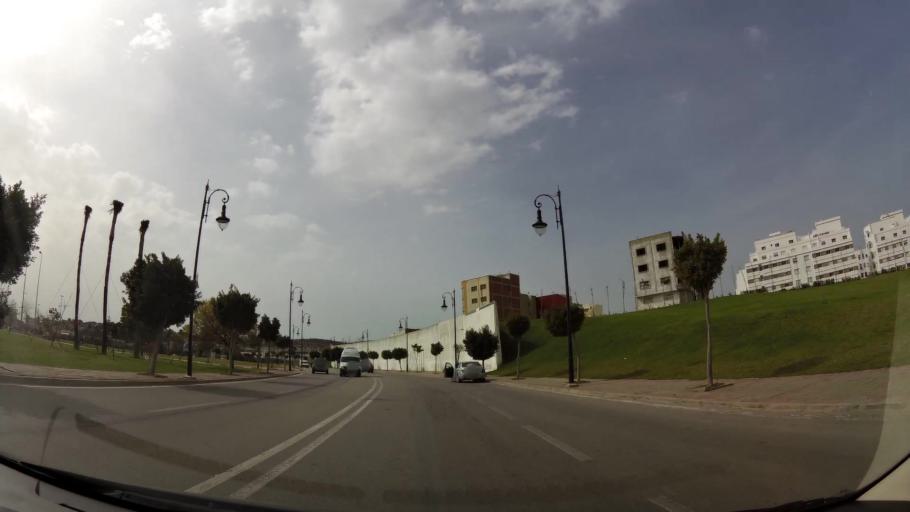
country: MA
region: Tanger-Tetouan
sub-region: Tanger-Assilah
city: Boukhalef
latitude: 35.7434
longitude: -5.8565
